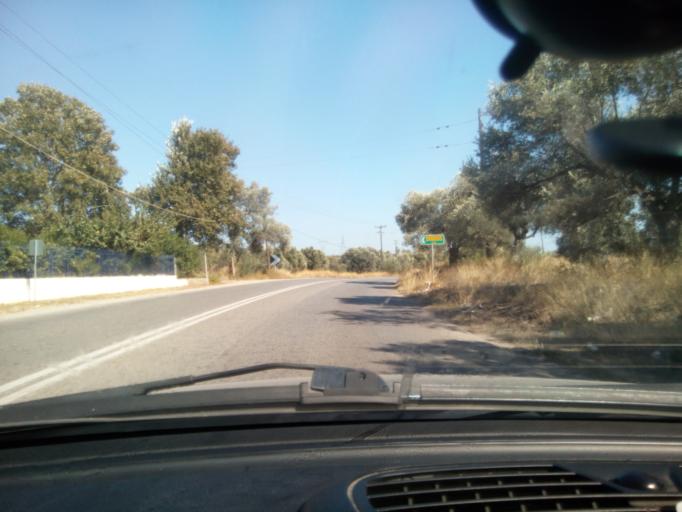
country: GR
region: Central Greece
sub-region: Nomos Evvoias
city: Filla
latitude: 38.4159
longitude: 23.7091
